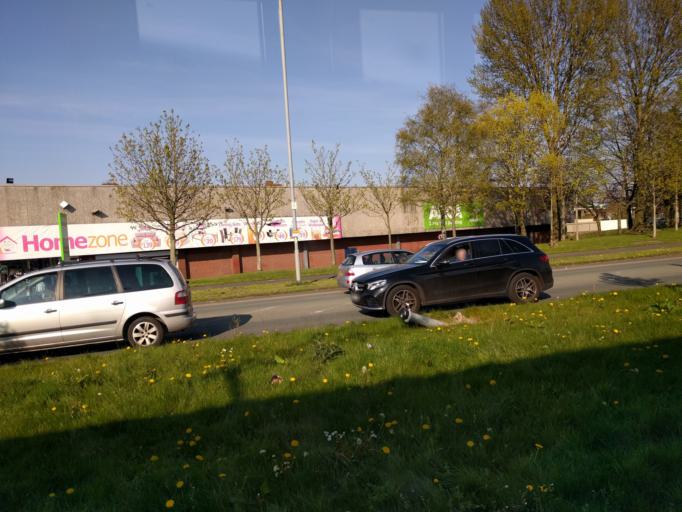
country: GB
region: England
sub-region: Manchester
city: Ringway
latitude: 53.3778
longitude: -2.2631
